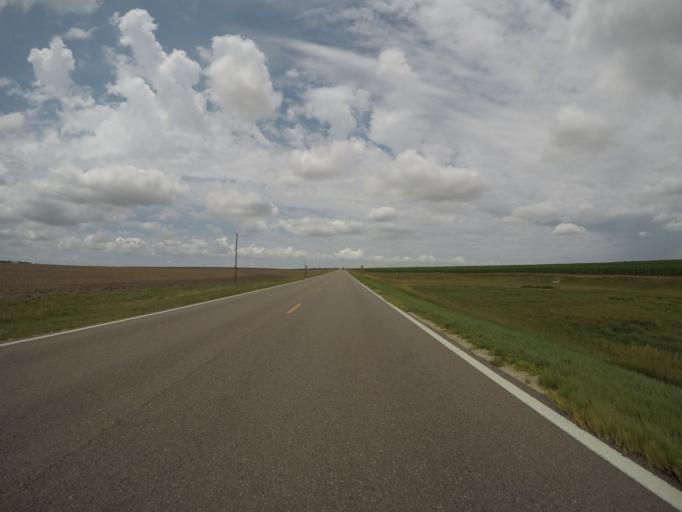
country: US
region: Kansas
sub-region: Rawlins County
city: Atwood
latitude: 39.7061
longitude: -101.0564
